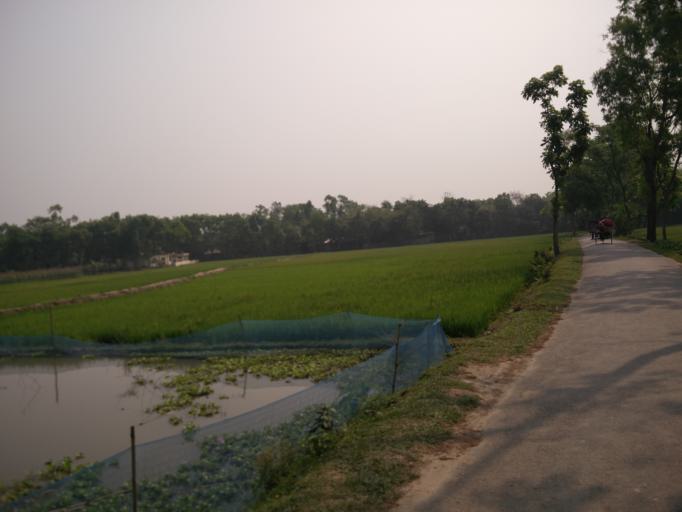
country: BD
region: Dhaka
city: Muktagacha
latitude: 24.9152
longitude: 90.2218
